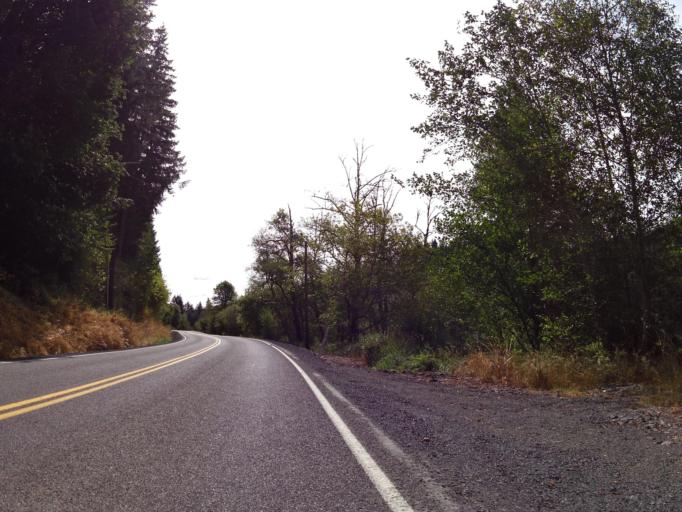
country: US
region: Washington
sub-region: Lewis County
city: Napavine
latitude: 46.5697
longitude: -122.9680
